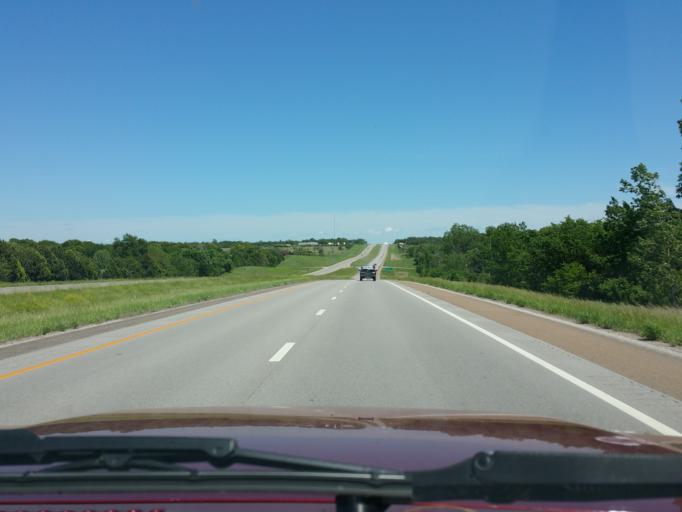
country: US
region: Kansas
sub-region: Pottawatomie County
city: Wamego
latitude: 39.2102
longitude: -96.3694
